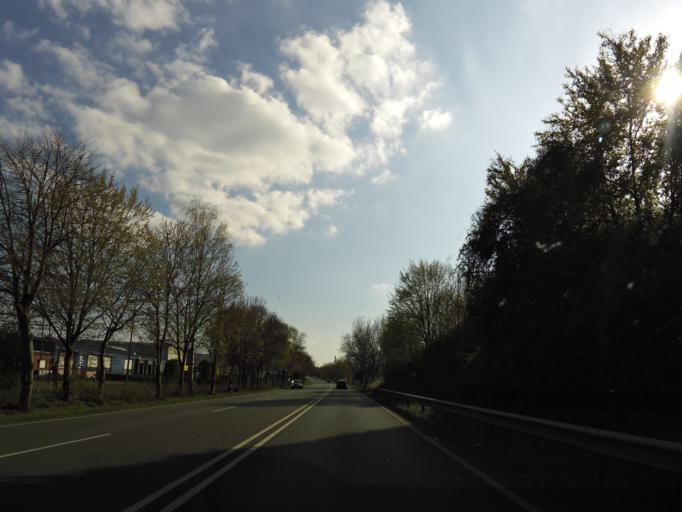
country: DE
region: North Rhine-Westphalia
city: Porta Westfalica
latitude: 52.2190
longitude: 8.8785
